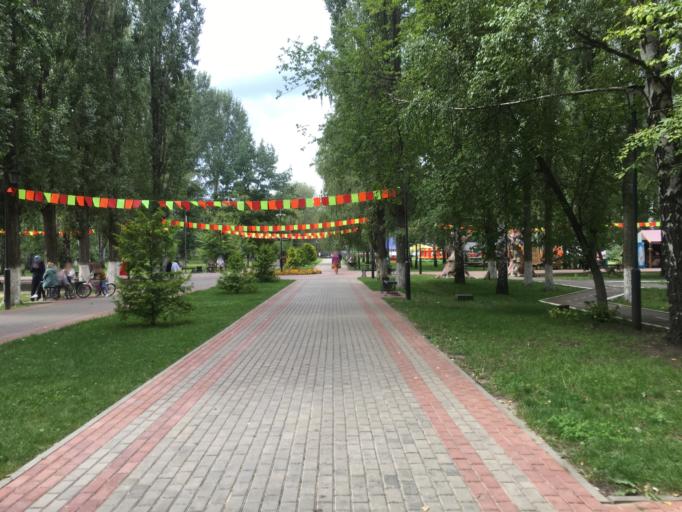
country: RU
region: Voronezj
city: Rossosh'
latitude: 50.1966
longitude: 39.5778
